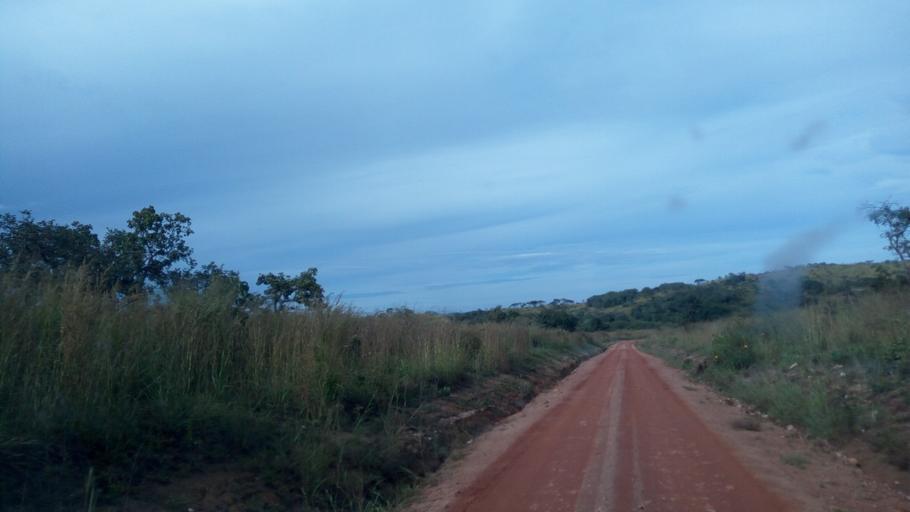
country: CD
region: Katanga
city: Kalemie
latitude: -6.2724
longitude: 29.0136
